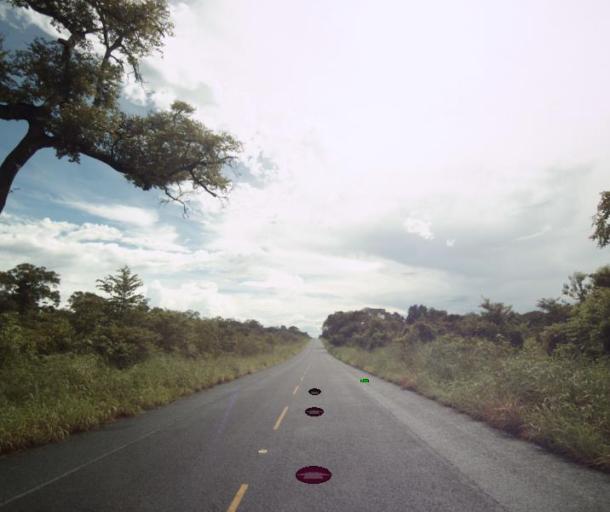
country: BR
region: Goias
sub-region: Sao Miguel Do Araguaia
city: Sao Miguel do Araguaia
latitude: -13.2990
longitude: -50.3182
